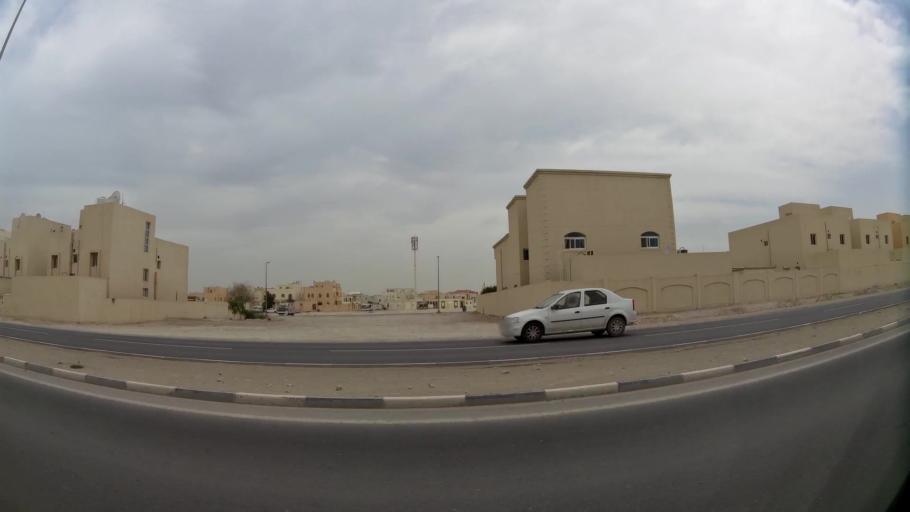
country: QA
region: Baladiyat ad Dawhah
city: Doha
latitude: 25.2235
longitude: 51.4691
